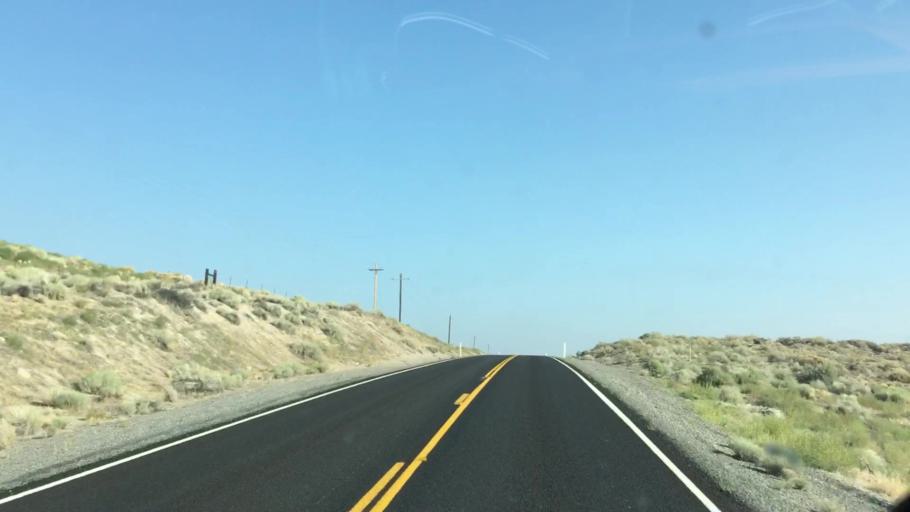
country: US
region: Nevada
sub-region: Lyon County
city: Fernley
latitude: 39.7629
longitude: -119.3403
